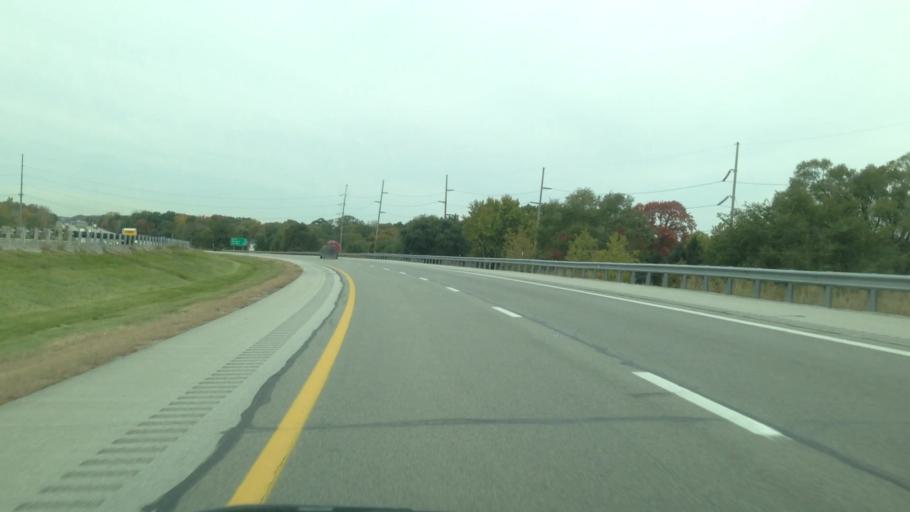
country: US
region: Ohio
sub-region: Fulton County
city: Swanton
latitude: 41.6026
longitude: -83.8097
